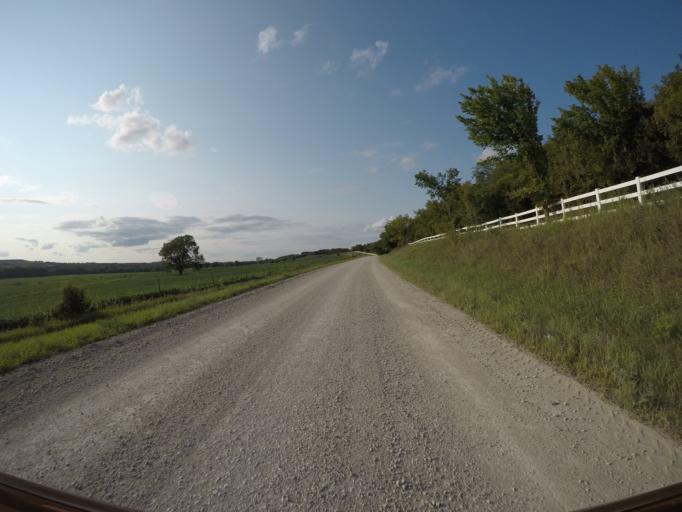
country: US
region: Kansas
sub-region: Wabaunsee County
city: Alma
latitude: 38.9380
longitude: -96.2354
